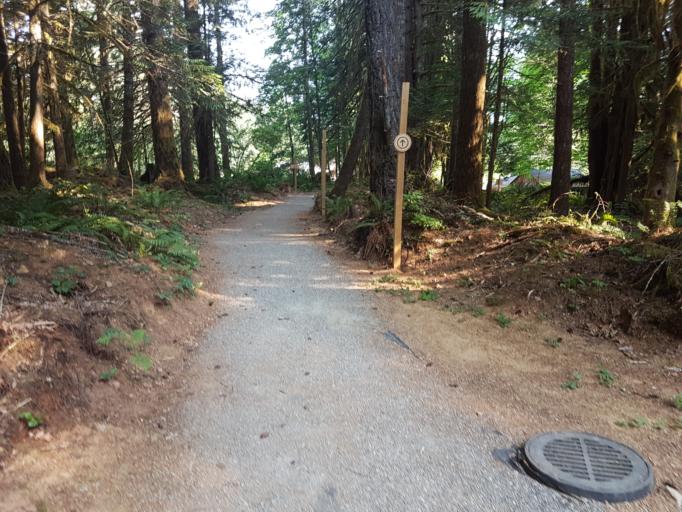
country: CA
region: British Columbia
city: Port Alberni
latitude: 49.3092
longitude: -124.8279
